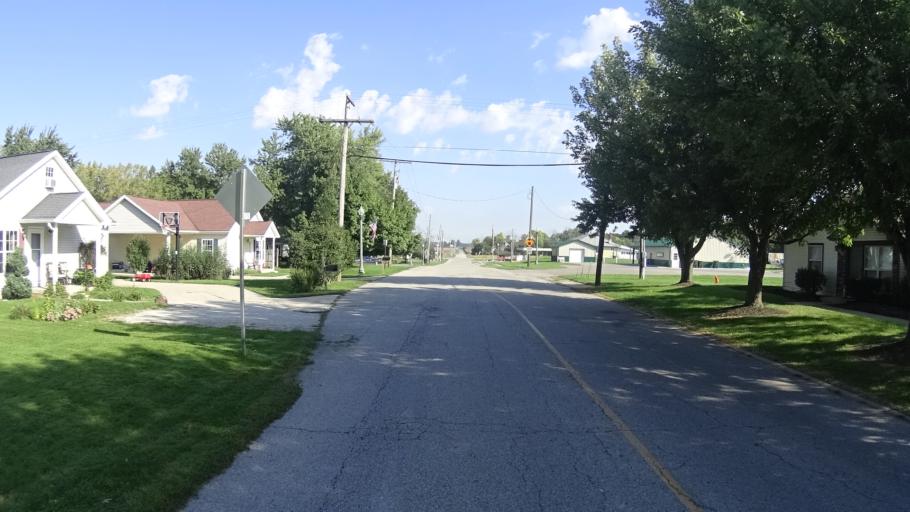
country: US
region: Indiana
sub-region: Madison County
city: Lapel
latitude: 40.0745
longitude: -85.8488
